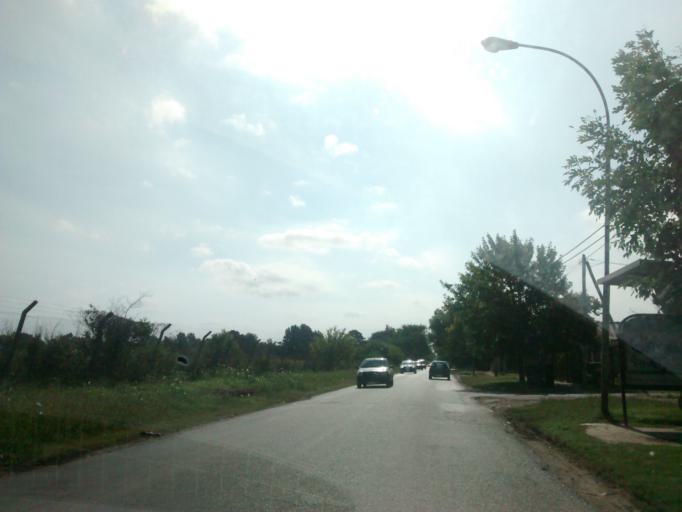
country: AR
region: Buenos Aires
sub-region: Partido de La Plata
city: La Plata
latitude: -34.9605
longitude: -57.8892
